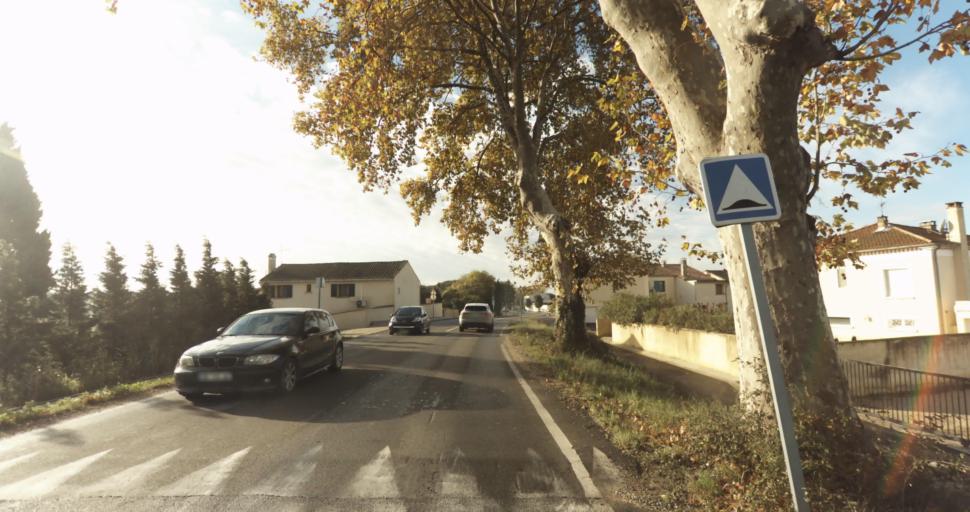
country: FR
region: Provence-Alpes-Cote d'Azur
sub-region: Departement des Bouches-du-Rhone
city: Rognonas
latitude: 43.9071
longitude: 4.8045
